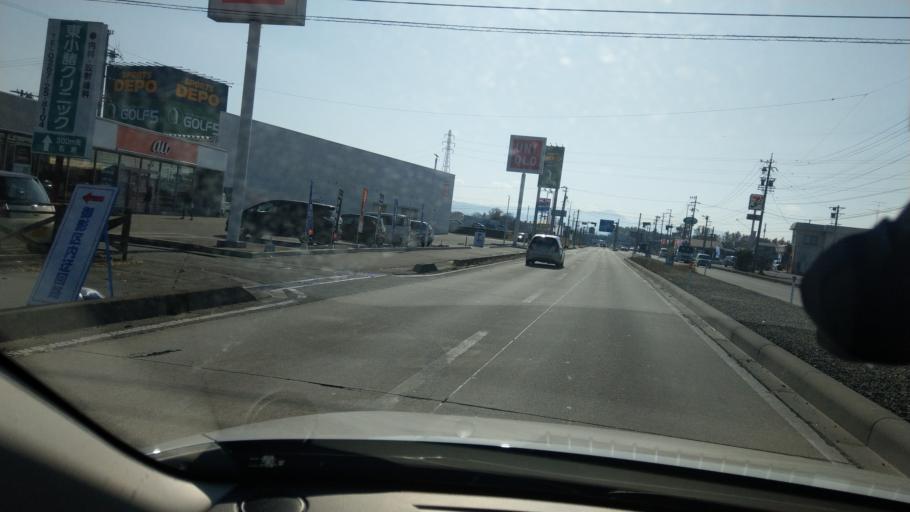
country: JP
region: Nagano
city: Komoro
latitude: 36.2988
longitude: 138.4677
